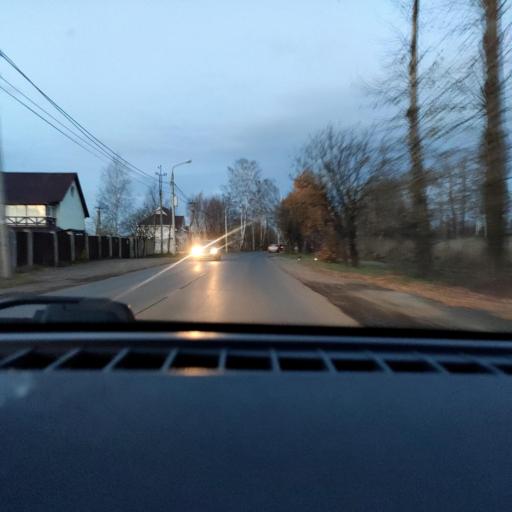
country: RU
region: Perm
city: Perm
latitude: 58.0490
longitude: 56.3446
